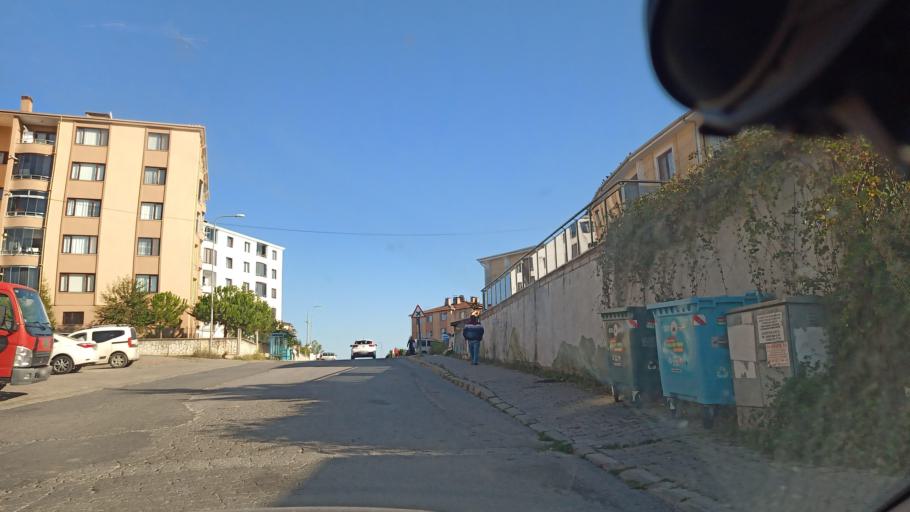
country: TR
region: Kocaeli
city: Kaymaz
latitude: 40.8593
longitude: 30.2888
